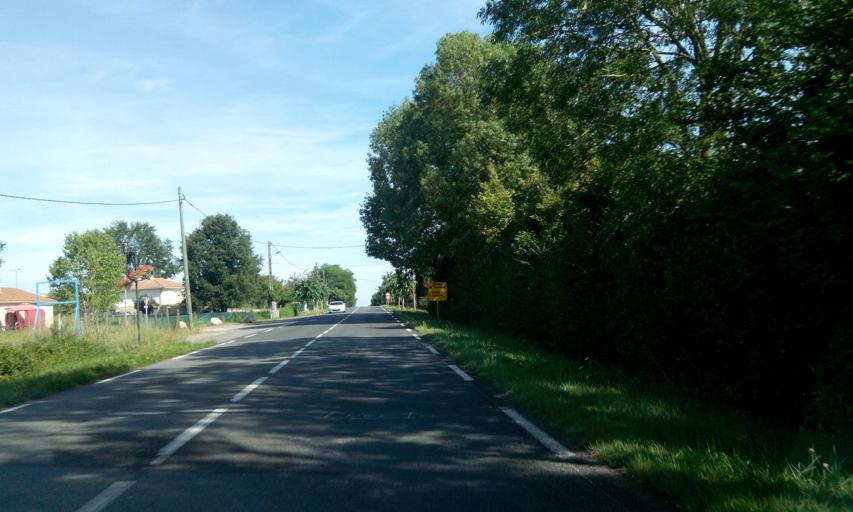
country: FR
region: Poitou-Charentes
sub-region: Departement de la Charente
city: Confolens
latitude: 45.9595
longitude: 0.7018
